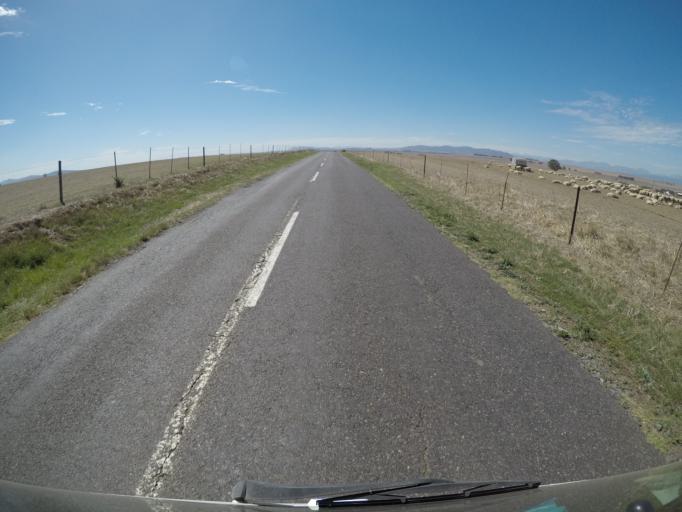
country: ZA
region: Western Cape
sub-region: City of Cape Town
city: Atlantis
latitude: -33.6861
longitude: 18.5988
